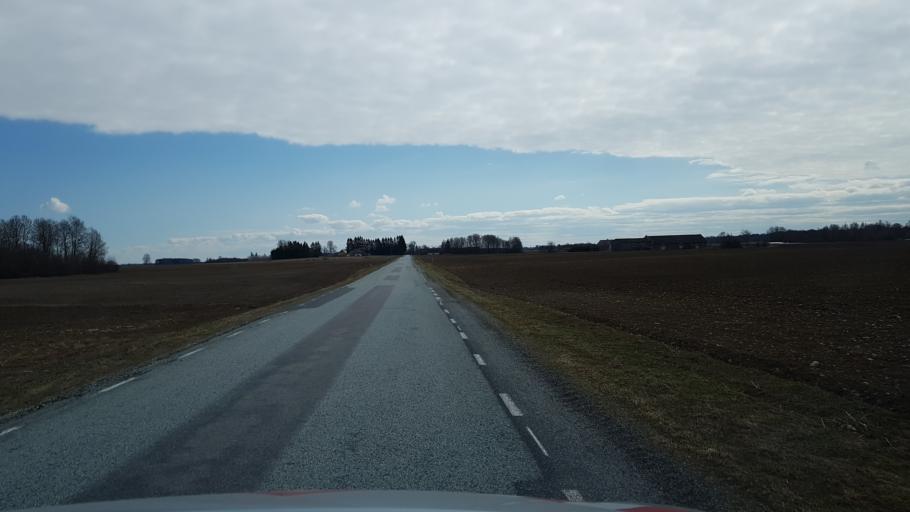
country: EE
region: Laeaene-Virumaa
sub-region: Haljala vald
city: Haljala
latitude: 59.4228
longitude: 26.2323
